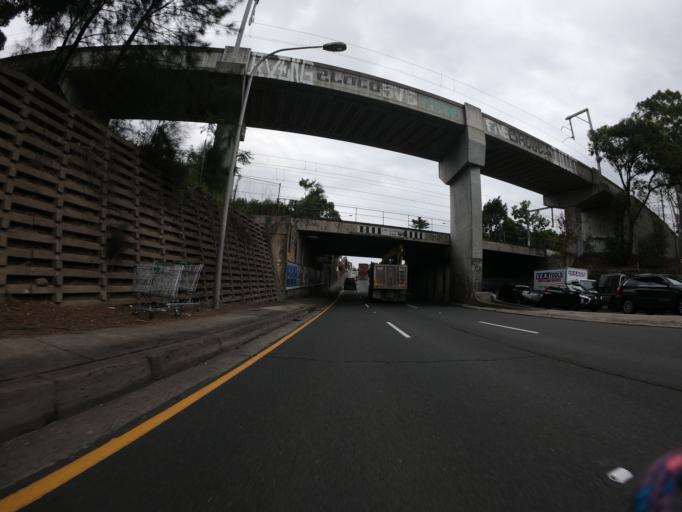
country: AU
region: New South Wales
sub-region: Parramatta
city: Harris Park
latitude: -33.8291
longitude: 151.0045
